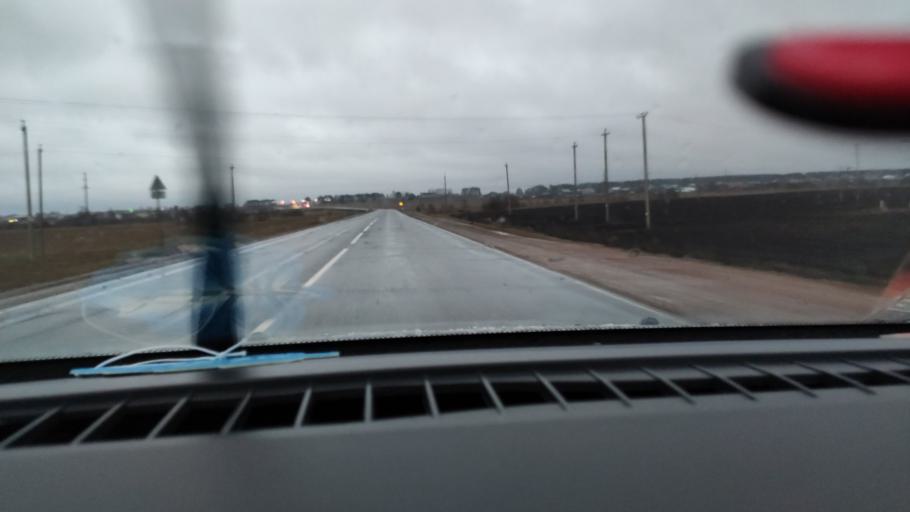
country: RU
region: Udmurtiya
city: Alnashi
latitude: 56.1863
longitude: 52.4575
